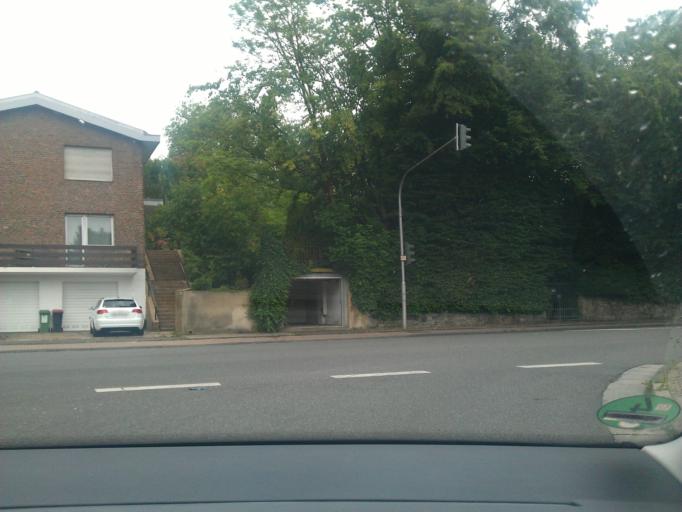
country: DE
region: North Rhine-Westphalia
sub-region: Regierungsbezirk Koln
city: Aachen
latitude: 50.7585
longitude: 6.0634
